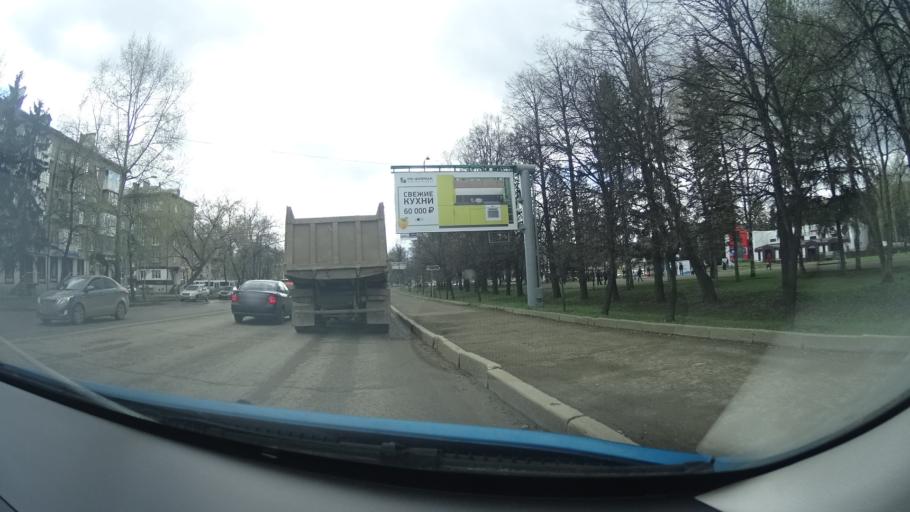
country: RU
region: Bashkortostan
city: Ufa
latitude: 54.8143
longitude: 56.0904
